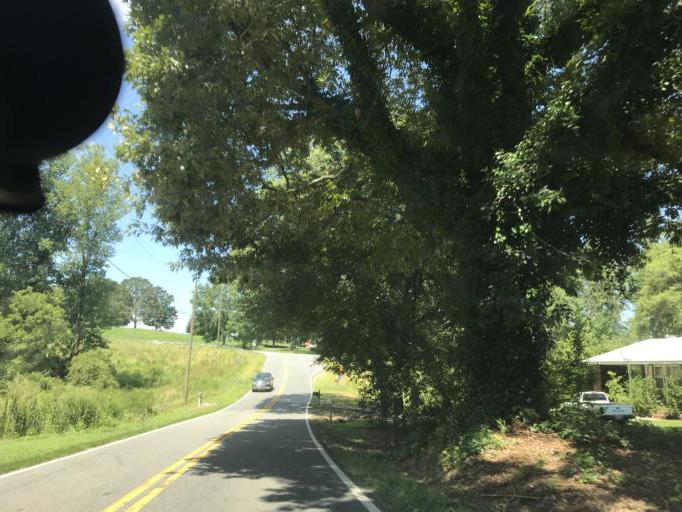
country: US
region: Georgia
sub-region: Forsyth County
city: Cumming
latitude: 34.2804
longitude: -84.0936
